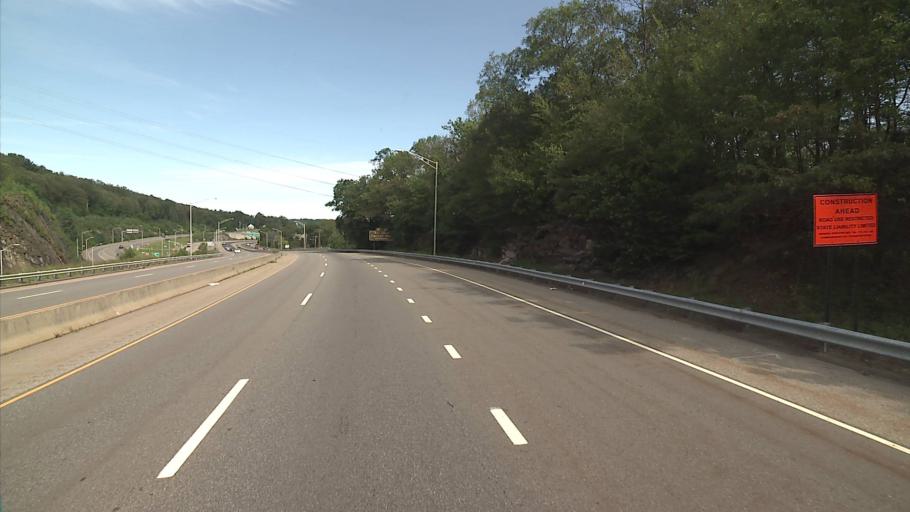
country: US
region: Connecticut
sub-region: New London County
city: Norwich
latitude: 41.5571
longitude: -72.1193
